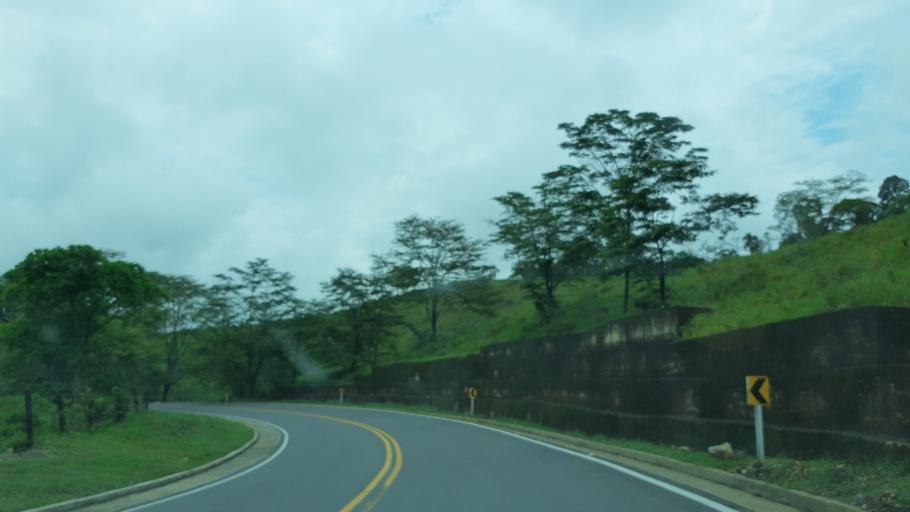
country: CO
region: Casanare
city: Sabanalarga
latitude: 4.7690
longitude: -73.0301
